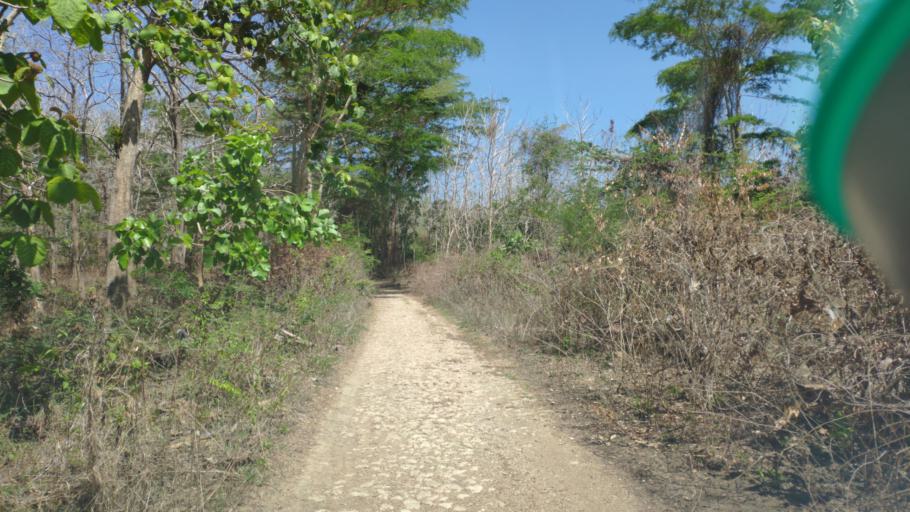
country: ID
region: Central Java
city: Suruhan
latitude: -7.0072
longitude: 111.5450
